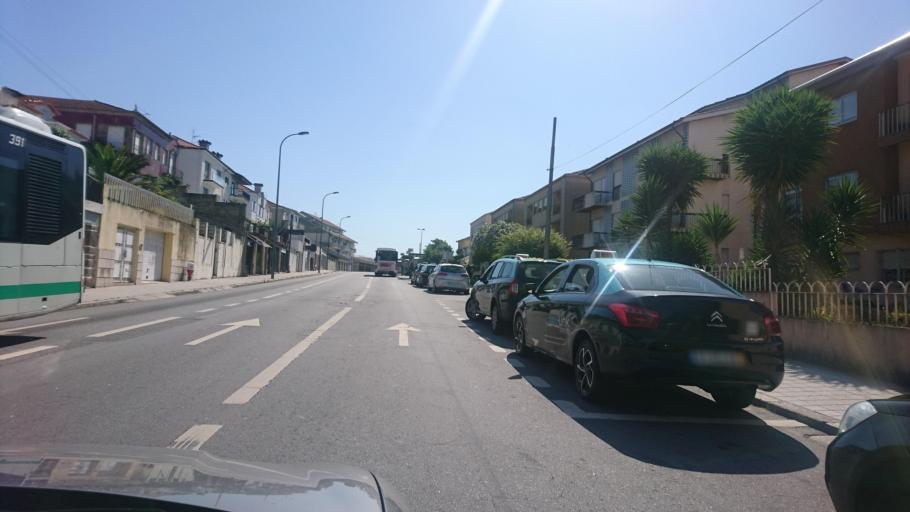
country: PT
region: Porto
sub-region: Gondomar
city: Rio Tinto
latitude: 41.1660
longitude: -8.5703
